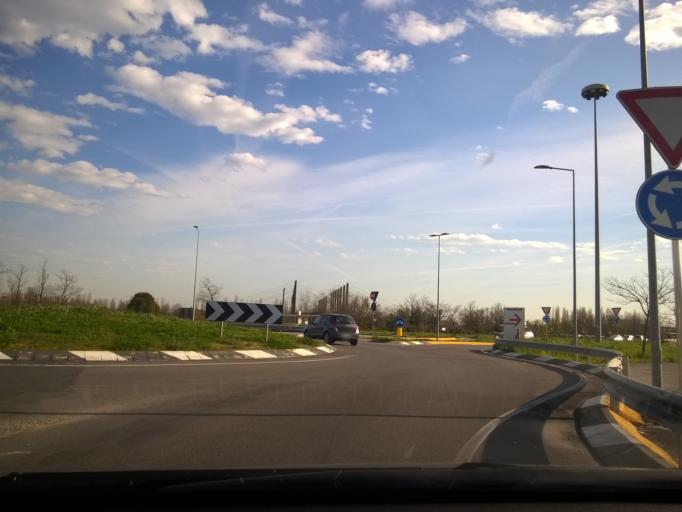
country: IT
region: Veneto
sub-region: Provincia di Treviso
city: Lancenigo-Villorba
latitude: 45.7425
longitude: 12.2544
